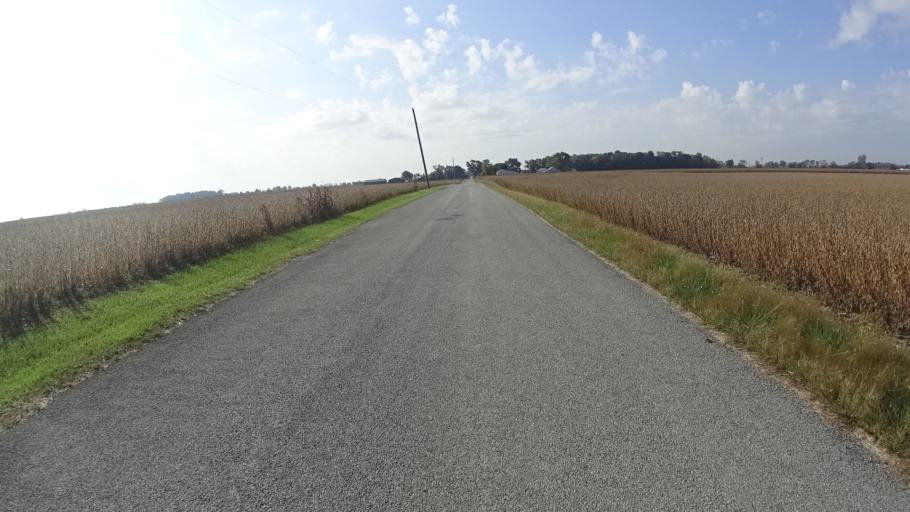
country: US
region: Indiana
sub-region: Madison County
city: Lapel
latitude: 40.0382
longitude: -85.8243
